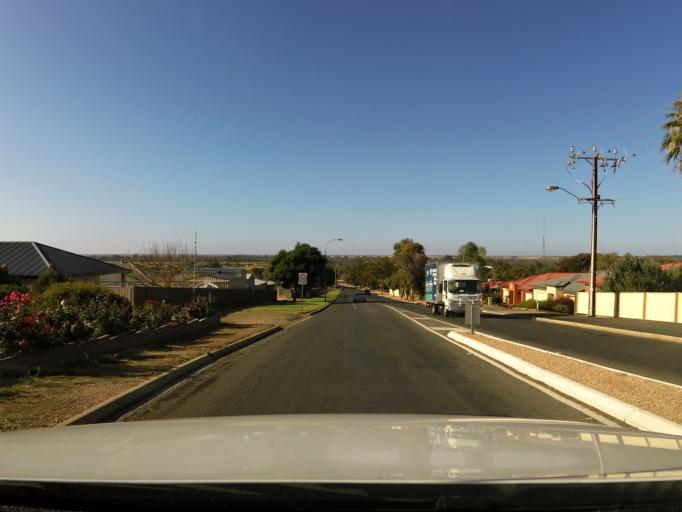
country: AU
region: South Australia
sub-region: Berri and Barmera
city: Berri
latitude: -34.2731
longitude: 140.6071
